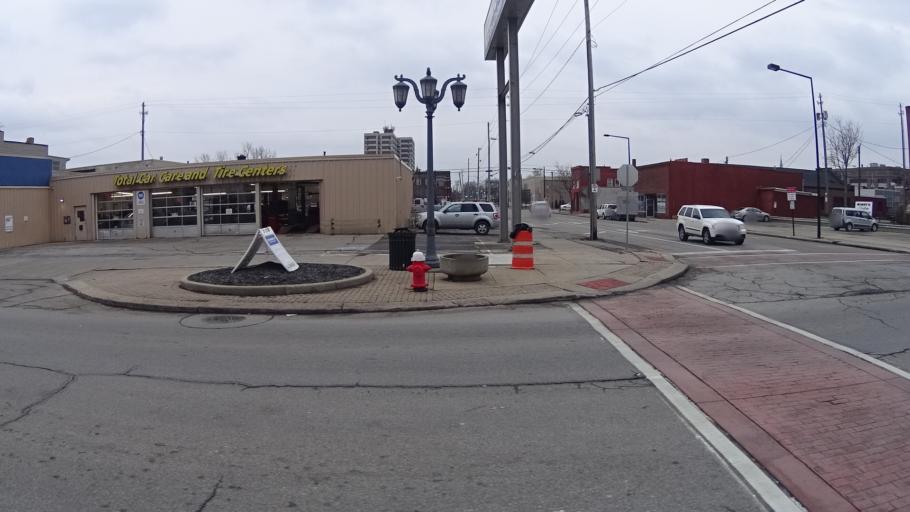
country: US
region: Ohio
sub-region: Lorain County
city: Elyria
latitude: 41.3677
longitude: -82.1039
